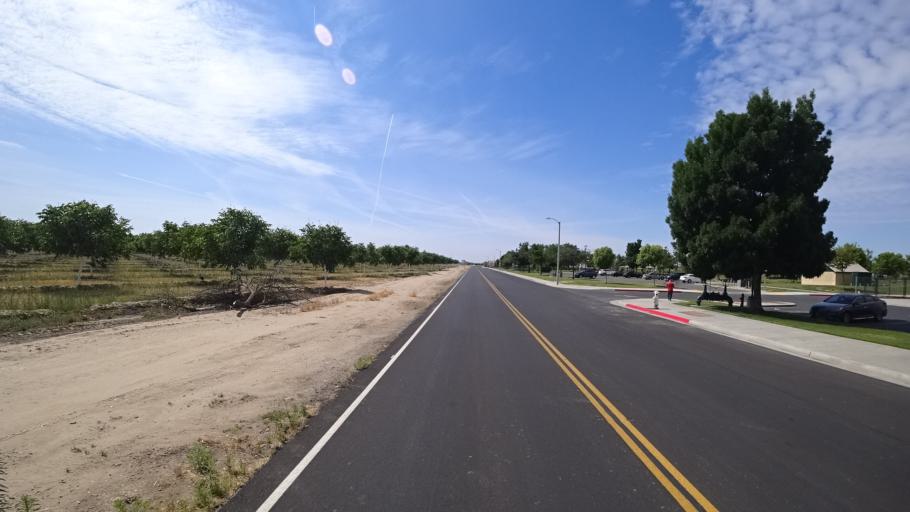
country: US
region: California
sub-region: Kings County
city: Hanford
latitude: 36.3484
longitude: -119.6244
